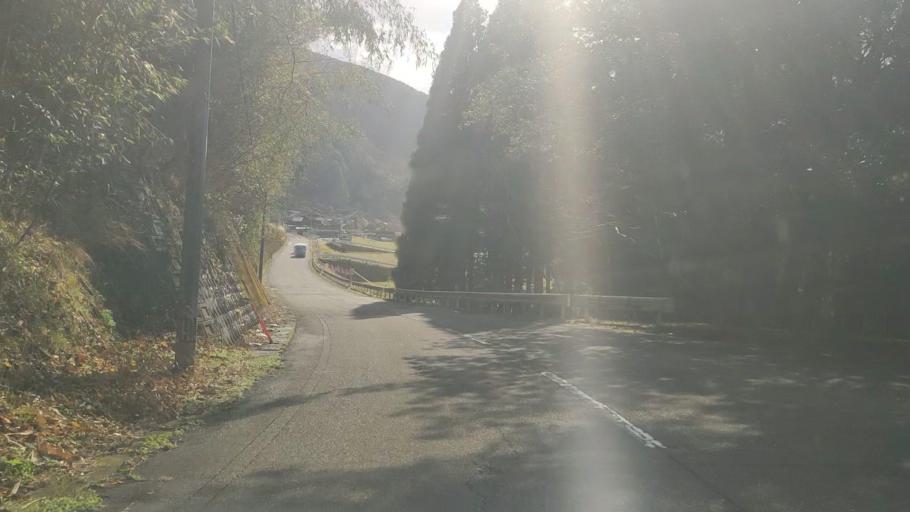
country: JP
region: Kumamoto
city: Hitoyoshi
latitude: 32.3169
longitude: 130.8440
